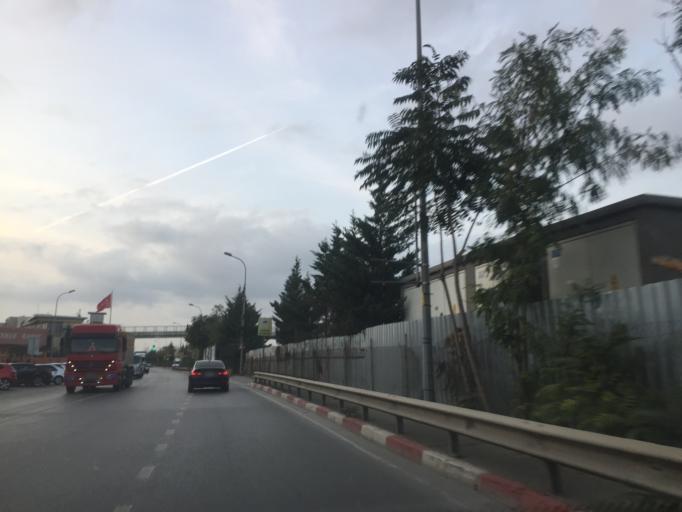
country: TR
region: Istanbul
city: Sultanbeyli
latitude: 40.9688
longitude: 29.2688
